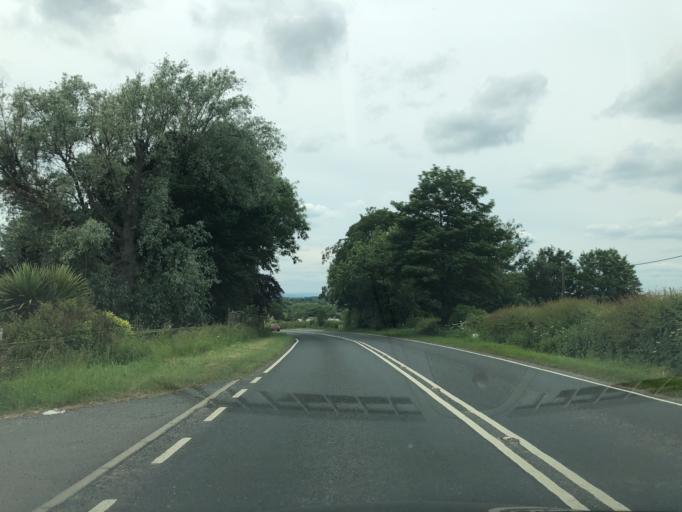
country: GB
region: England
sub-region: North Yorkshire
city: Thirsk
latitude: 54.2346
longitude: -1.3161
